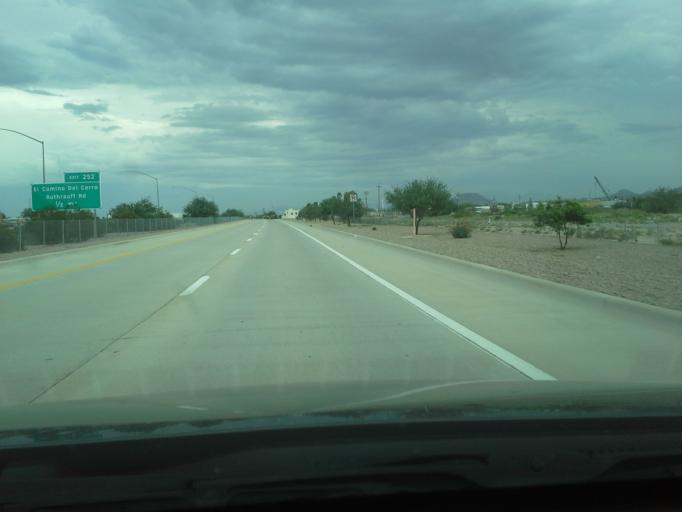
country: US
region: Arizona
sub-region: Pima County
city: Flowing Wells
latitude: 32.3040
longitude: -111.0390
